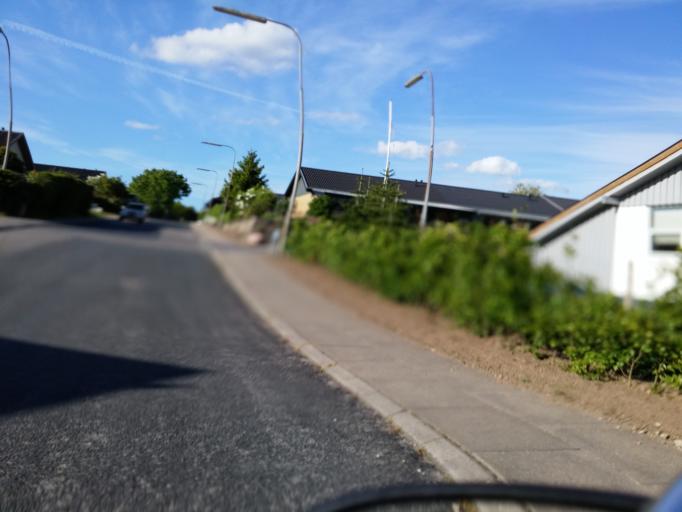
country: DK
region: South Denmark
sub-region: Odense Kommune
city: Seden
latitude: 55.3991
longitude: 10.4524
